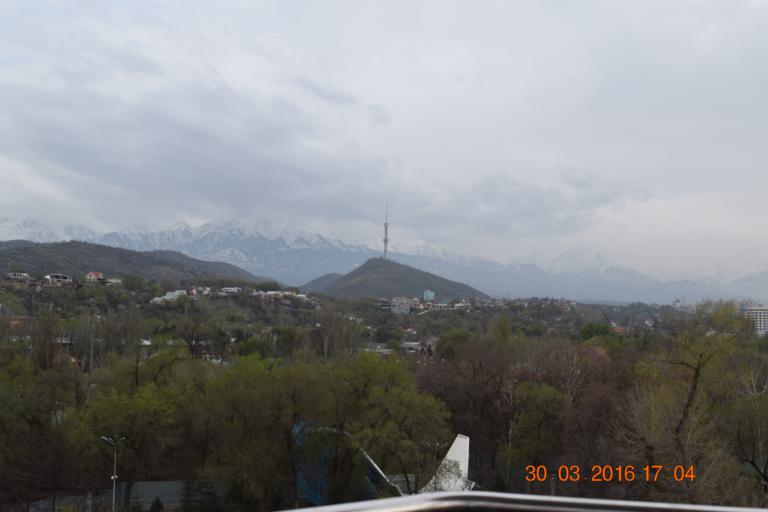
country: KZ
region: Almaty Qalasy
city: Almaty
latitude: 43.2618
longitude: 76.9717
